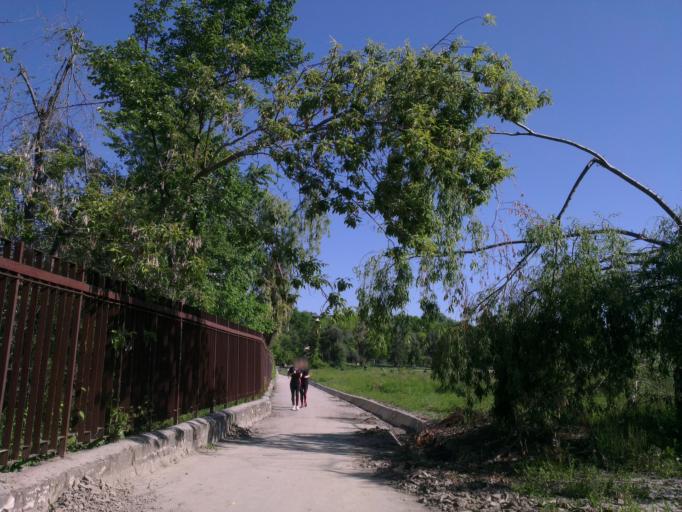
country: MD
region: Chisinau
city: Chisinau
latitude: 47.0159
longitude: 28.8070
